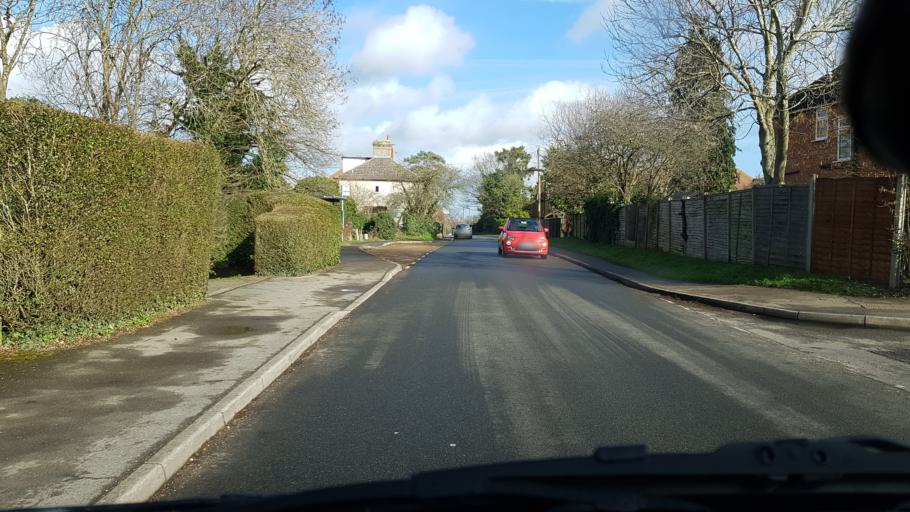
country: GB
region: England
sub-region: Surrey
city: Guildford
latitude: 51.2558
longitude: -0.6007
